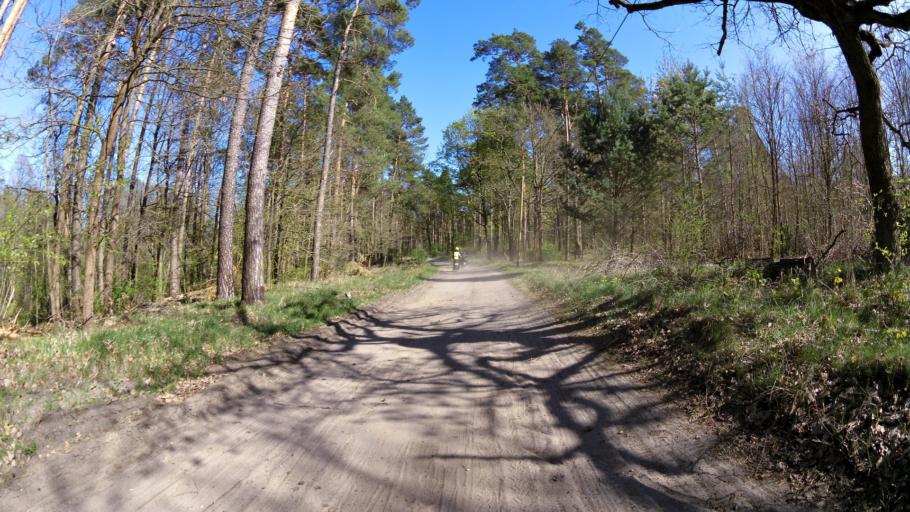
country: DE
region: Brandenburg
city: Grunheide
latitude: 52.4092
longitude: 13.8281
